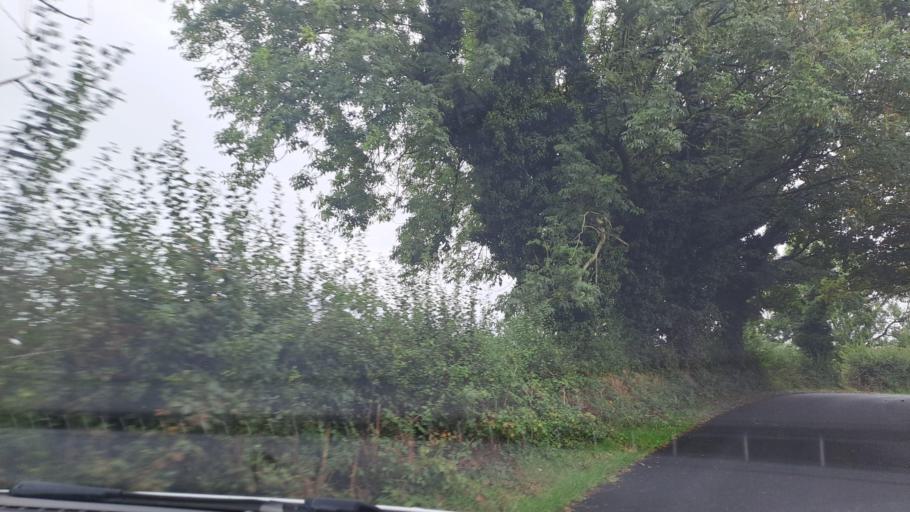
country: IE
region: Ulster
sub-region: An Cabhan
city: Kingscourt
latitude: 53.9805
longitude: -6.8138
